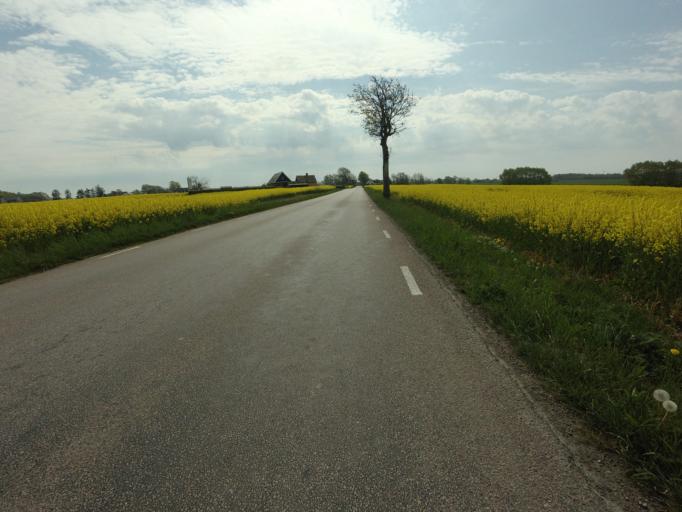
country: SE
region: Skane
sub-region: Hoganas Kommun
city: Hoganas
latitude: 56.1982
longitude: 12.5982
